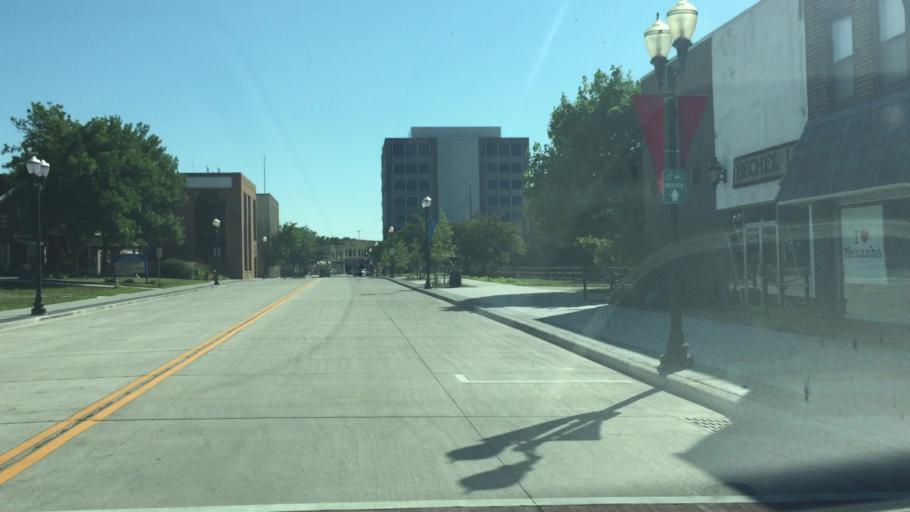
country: US
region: Wisconsin
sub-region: Winnebago County
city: Menasha
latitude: 44.1999
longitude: -88.4516
